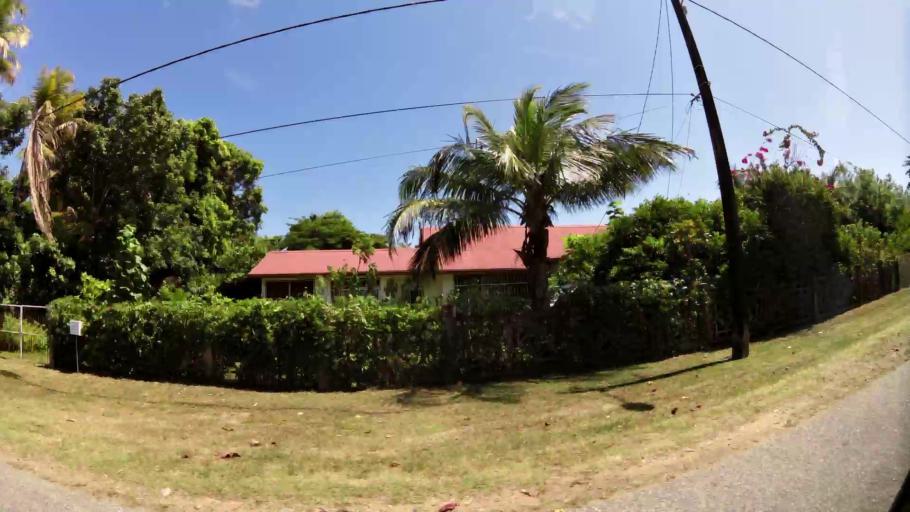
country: GF
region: Guyane
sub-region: Guyane
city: Cayenne
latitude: 4.9438
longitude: -52.3196
